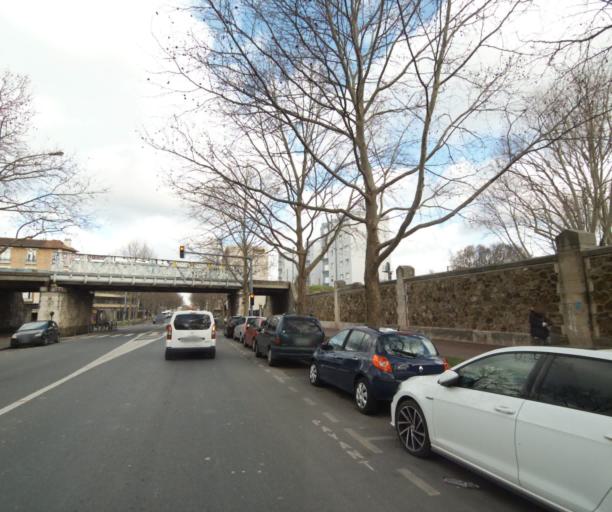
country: FR
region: Ile-de-France
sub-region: Paris
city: Saint-Ouen
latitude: 48.9100
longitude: 2.3442
